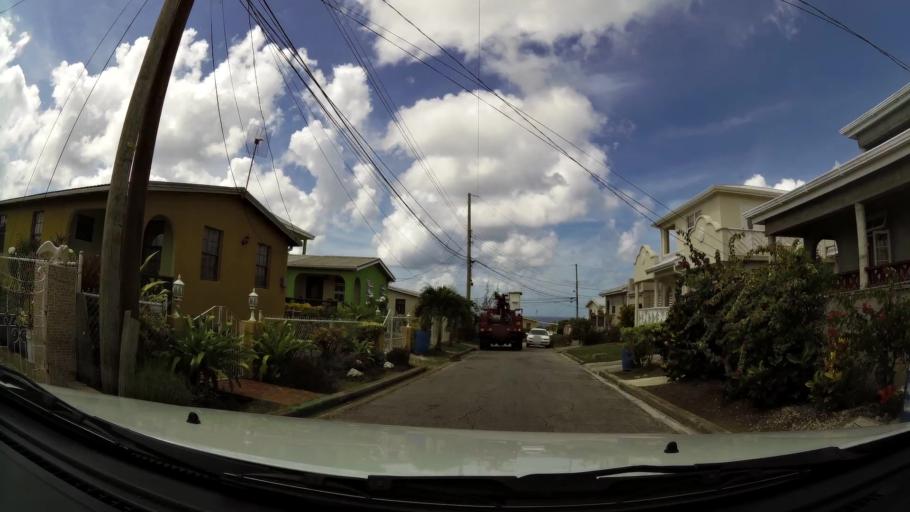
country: BB
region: Saint James
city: Holetown
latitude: 13.1505
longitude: -59.6271
